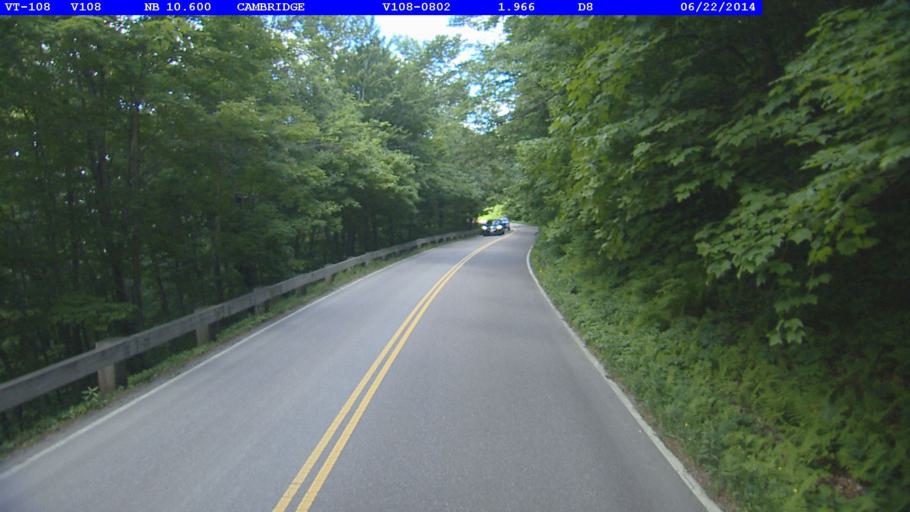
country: US
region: Vermont
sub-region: Lamoille County
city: Johnson
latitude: 44.5651
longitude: -72.7847
